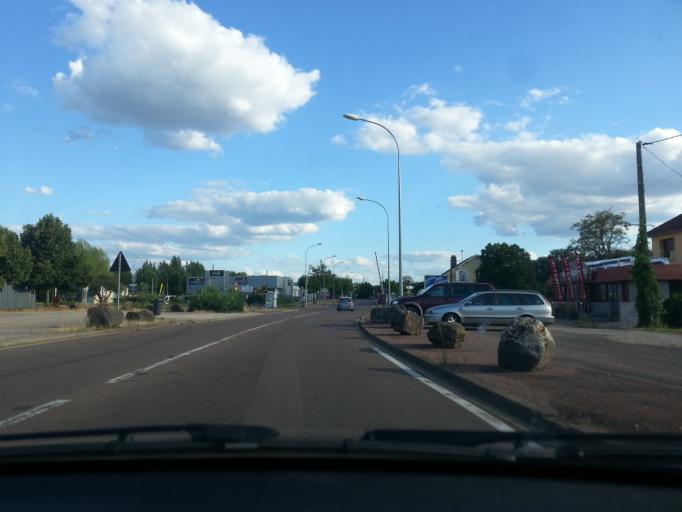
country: FR
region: Bourgogne
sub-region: Departement de Saone-et-Loire
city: Chalon-sur-Saone
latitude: 46.7717
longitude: 4.8591
